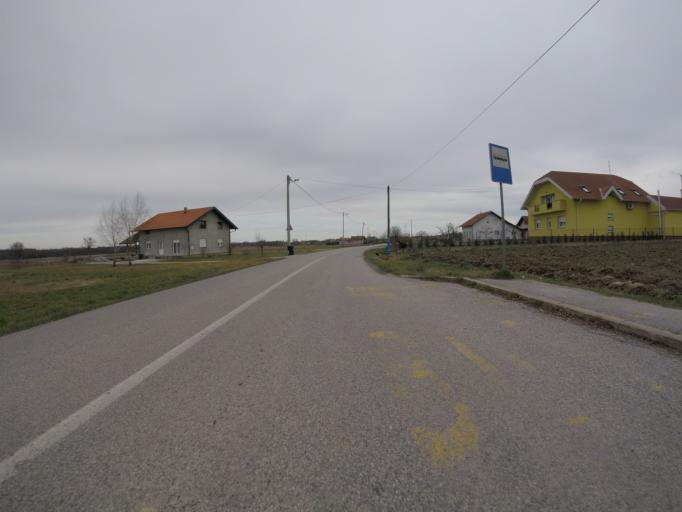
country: HR
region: Grad Zagreb
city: Strmec
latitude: 45.6672
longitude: 15.9305
